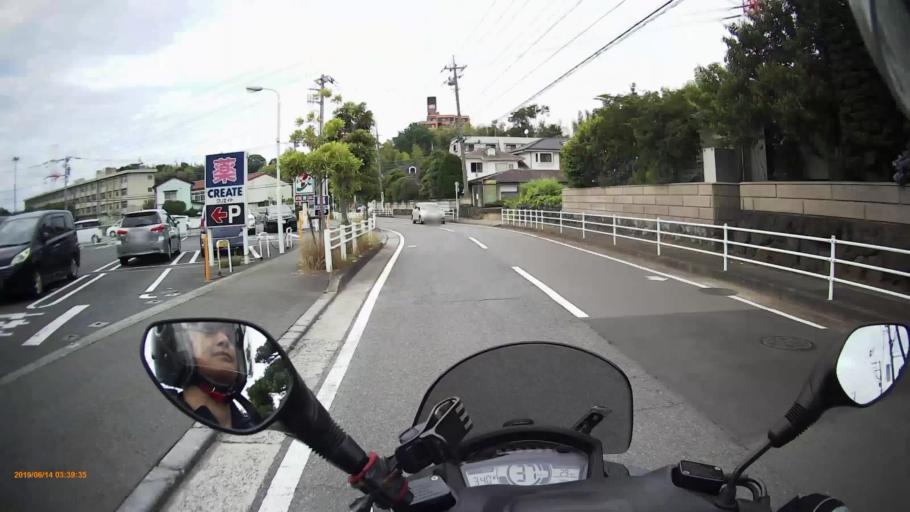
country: JP
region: Kanagawa
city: Minami-rinkan
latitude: 35.4170
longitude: 139.4482
